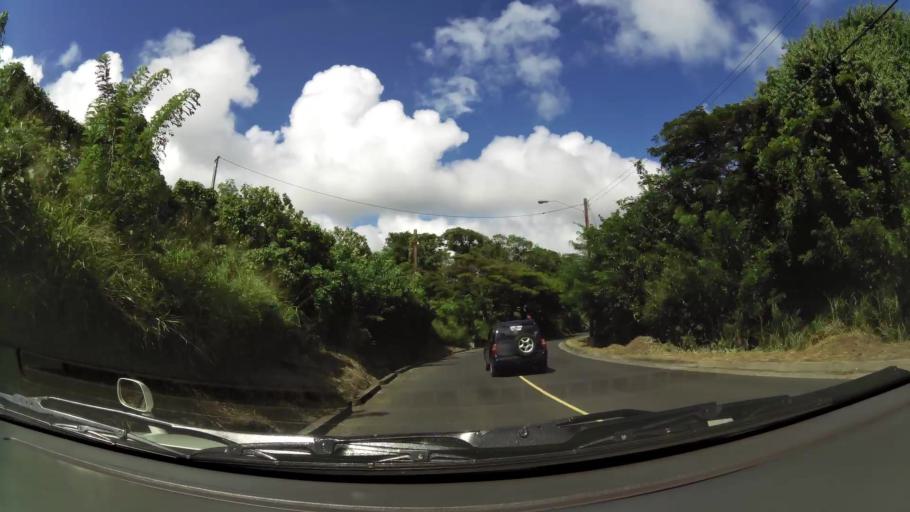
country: VC
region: Saint George
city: Kingstown
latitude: 13.1296
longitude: -61.1899
